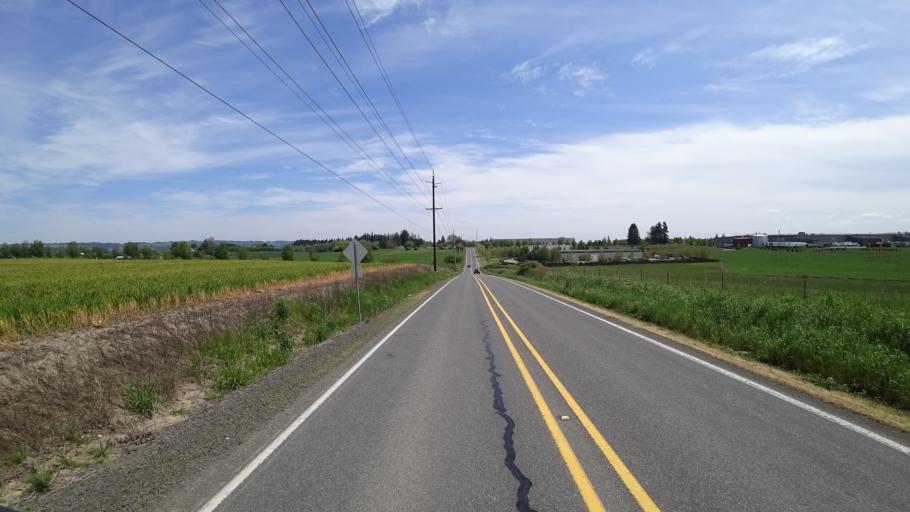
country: US
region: Oregon
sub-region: Washington County
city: Rockcreek
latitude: 45.5752
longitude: -122.9123
